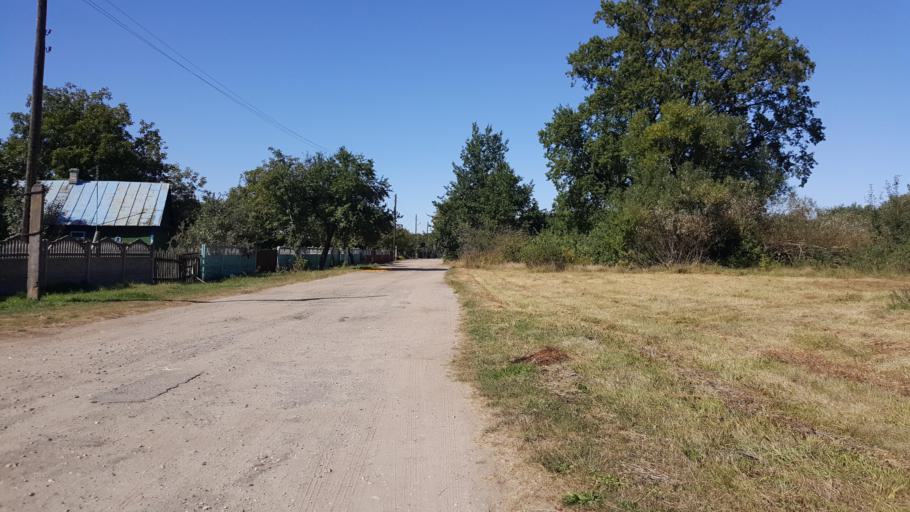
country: BY
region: Brest
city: Vysokaye
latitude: 52.2336
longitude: 23.5028
